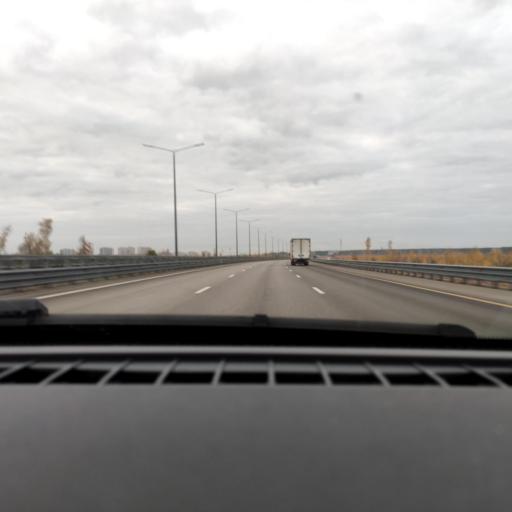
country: RU
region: Voronezj
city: Somovo
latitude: 51.7591
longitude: 39.3071
